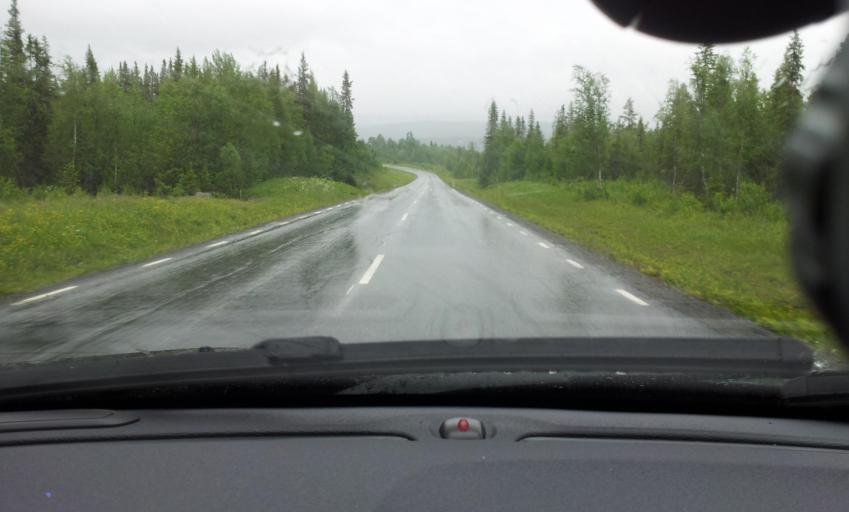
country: SE
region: Jaemtland
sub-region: Are Kommun
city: Are
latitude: 63.2936
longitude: 13.2317
